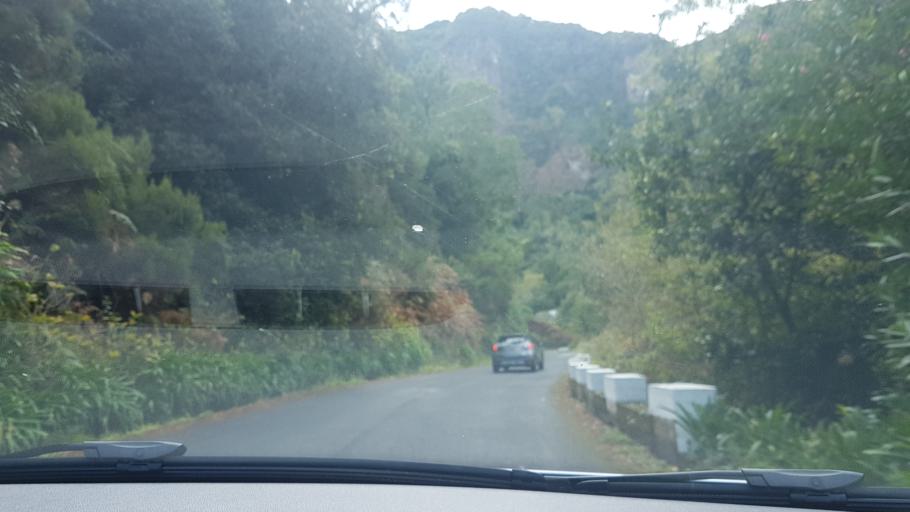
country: PT
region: Madeira
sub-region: Sao Vicente
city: Sao Vicente
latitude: 32.7671
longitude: -17.0268
